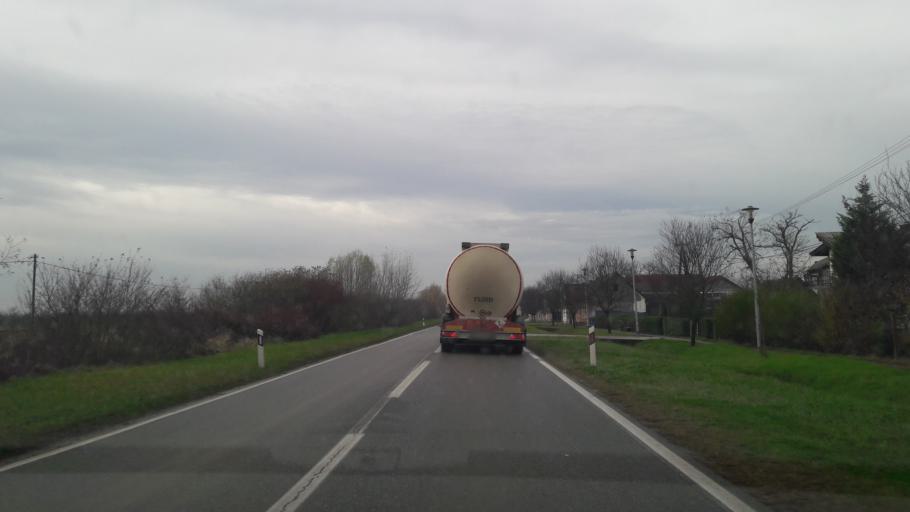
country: HR
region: Osjecko-Baranjska
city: Bizovac
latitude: 45.5848
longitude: 18.4390
